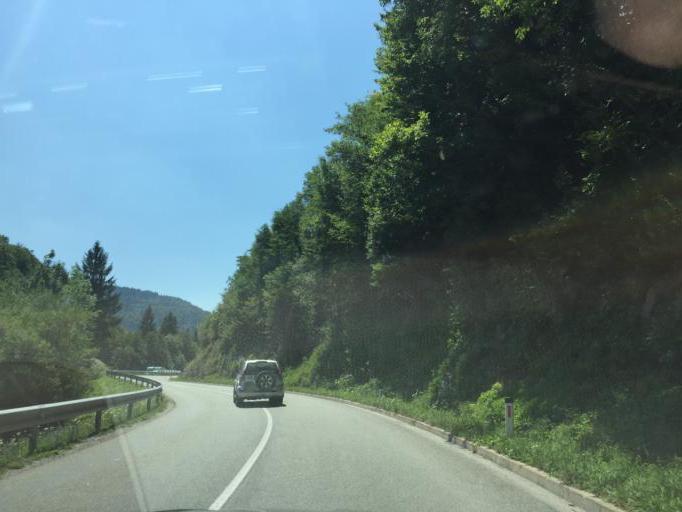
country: SI
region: Gorenja Vas-Poljane
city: Gorenja Vas
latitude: 46.1060
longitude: 14.1149
